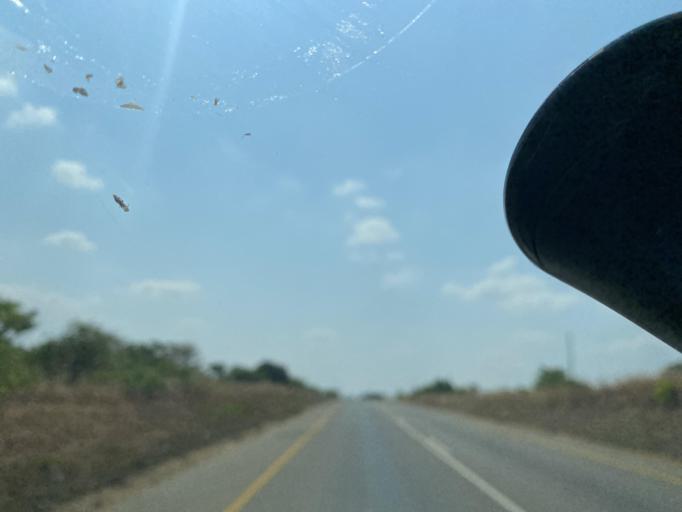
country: ZM
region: Lusaka
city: Chongwe
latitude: -15.5375
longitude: 28.6529
